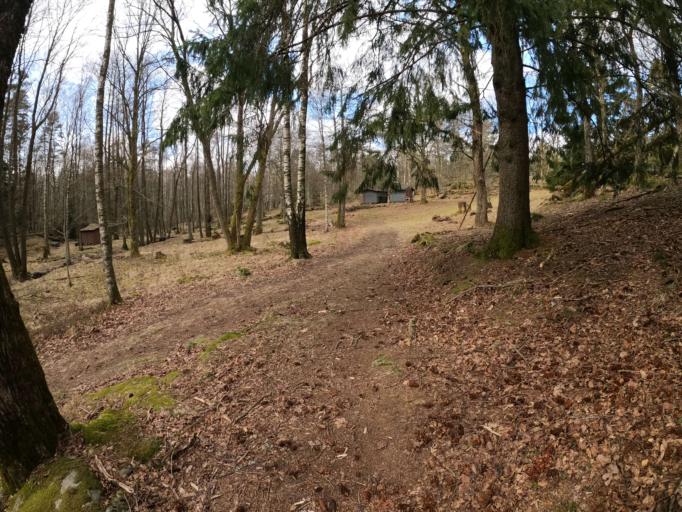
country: SE
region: Vaestra Goetaland
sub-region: Molndal
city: Kallered
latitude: 57.6313
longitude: 12.0864
